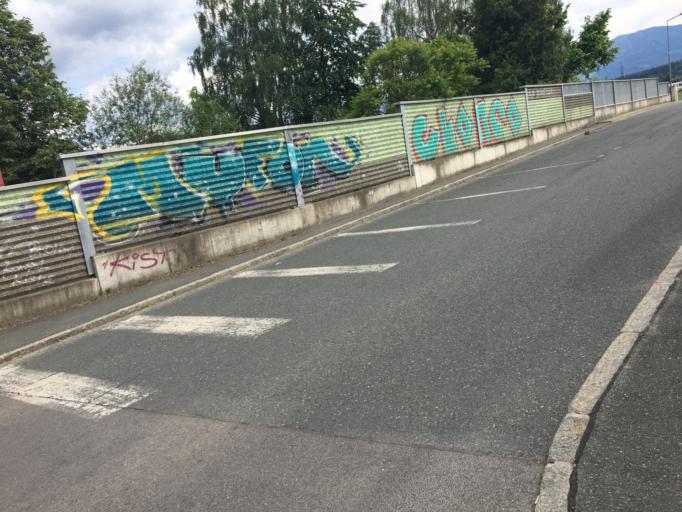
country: AT
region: Carinthia
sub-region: Klagenfurt am Woerthersee
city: Klagenfurt am Woerthersee
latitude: 46.6050
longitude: 14.2740
